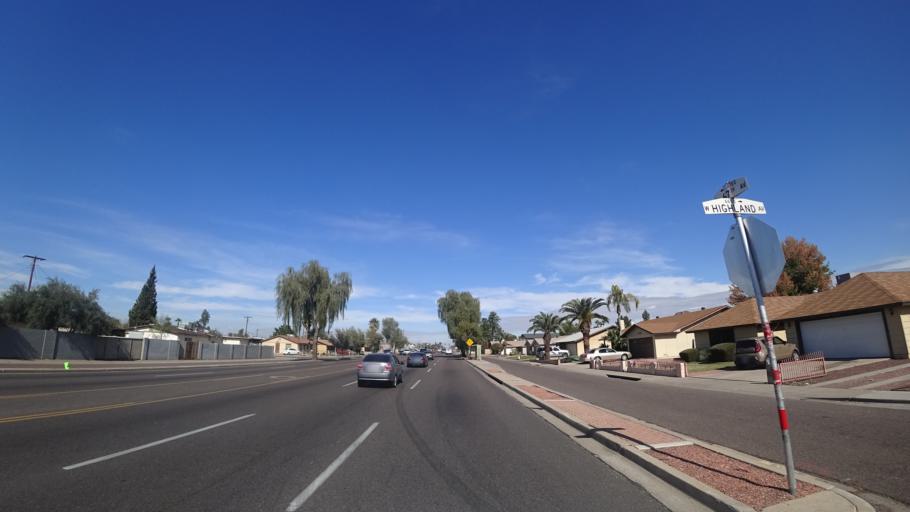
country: US
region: Arizona
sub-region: Maricopa County
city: Glendale
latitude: 33.5064
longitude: -112.2031
